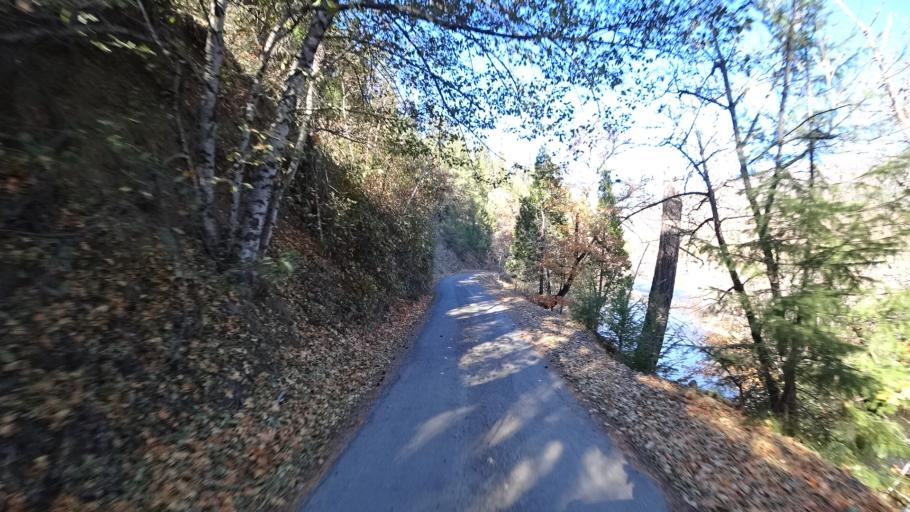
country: US
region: California
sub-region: Siskiyou County
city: Yreka
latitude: 41.8366
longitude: -122.8706
